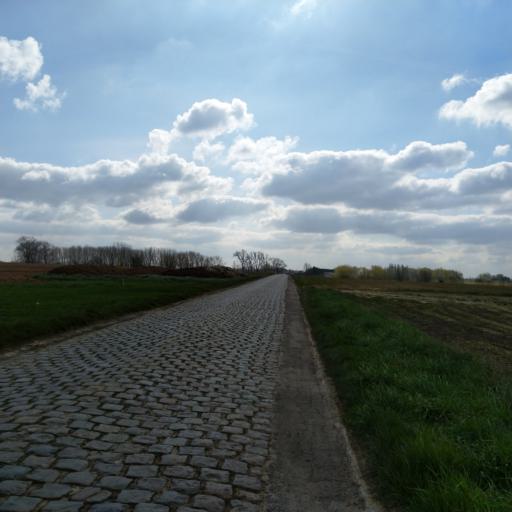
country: BE
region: Wallonia
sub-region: Province du Hainaut
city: Jurbise
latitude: 50.5507
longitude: 3.9514
